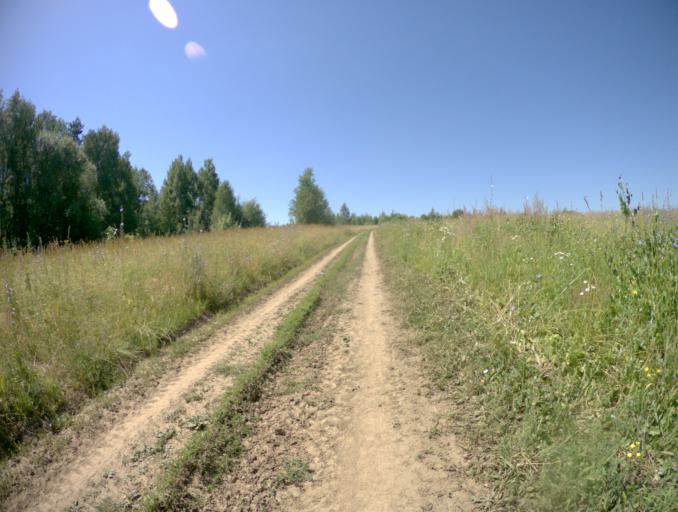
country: RU
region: Nizjnij Novgorod
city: Reshetikha
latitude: 56.1252
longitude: 43.2625
